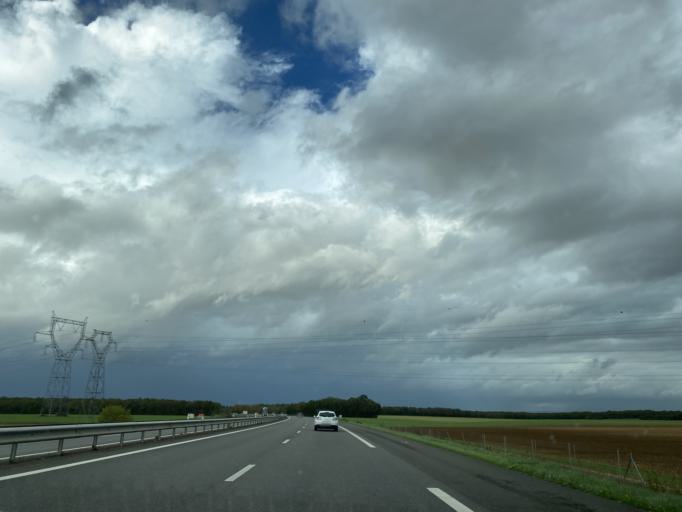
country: FR
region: Centre
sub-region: Departement du Cher
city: Plaimpied-Givaudins
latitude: 46.9690
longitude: 2.4251
